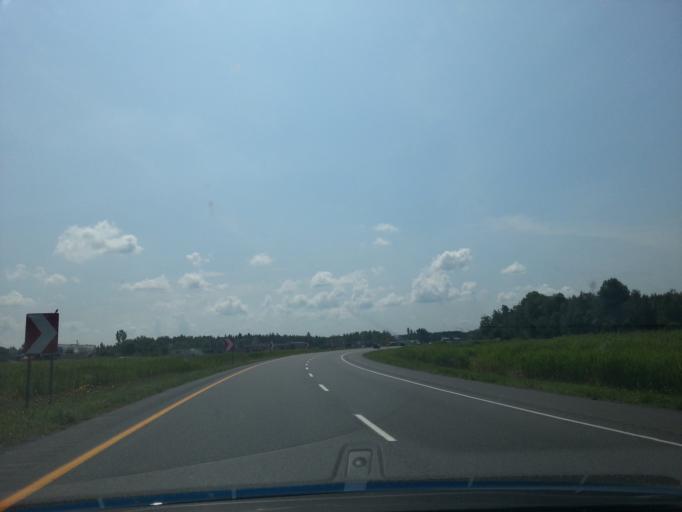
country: CA
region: Quebec
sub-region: Mauricie
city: Daveluyville
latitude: 46.2163
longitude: -72.0596
